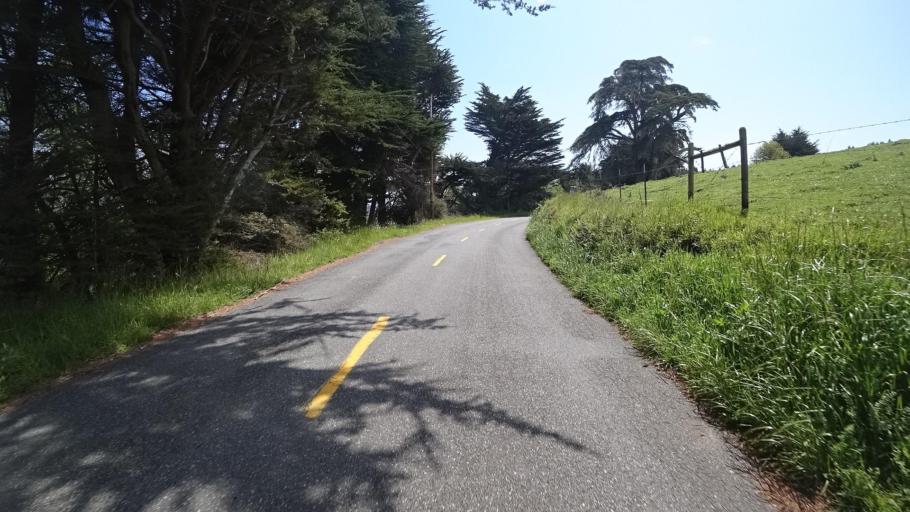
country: US
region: California
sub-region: Humboldt County
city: Humboldt Hill
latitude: 40.6761
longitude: -124.2243
